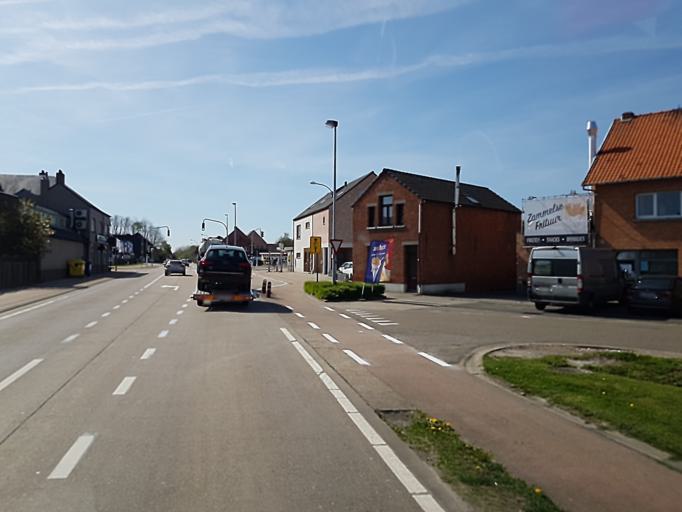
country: BE
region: Flanders
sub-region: Provincie Antwerpen
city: Westerlo
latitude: 51.0980
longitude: 4.9446
